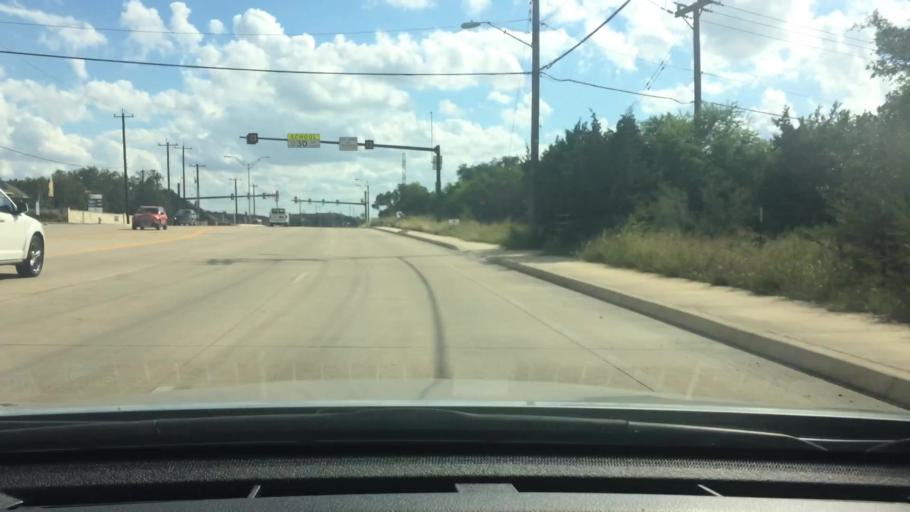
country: US
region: Texas
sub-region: Bexar County
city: Hollywood Park
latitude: 29.6400
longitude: -98.4249
